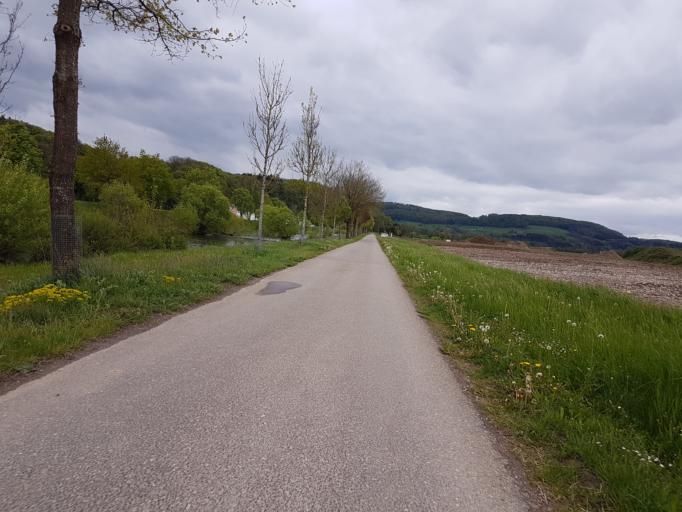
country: DE
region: Baden-Wuerttemberg
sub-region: Freiburg Region
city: Lauchringen
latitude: 47.6375
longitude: 8.3462
